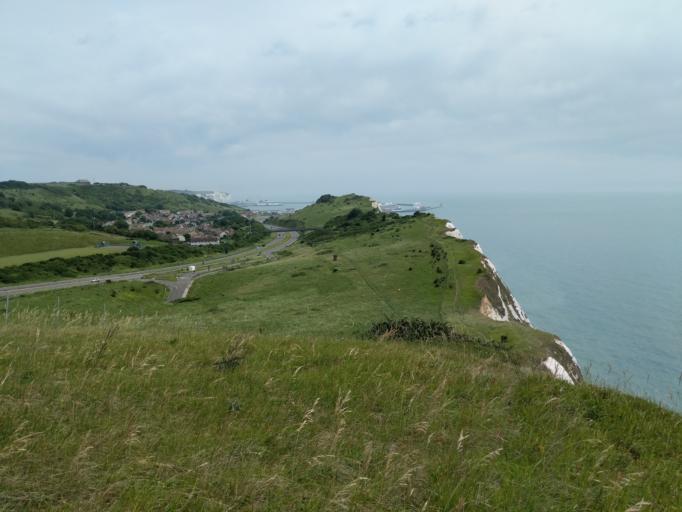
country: GB
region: England
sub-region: Kent
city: Dover
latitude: 51.1084
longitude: 1.2806
